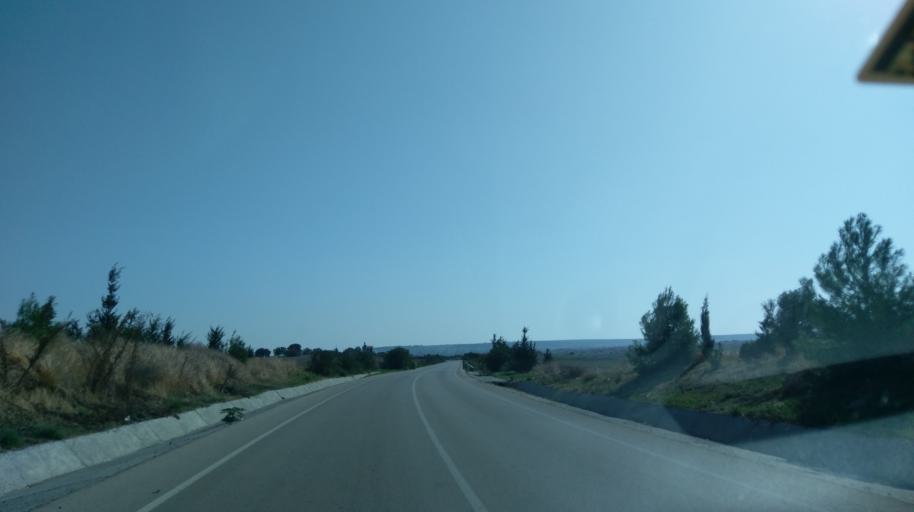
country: CY
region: Ammochostos
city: Leonarisso
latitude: 35.3909
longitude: 34.0090
